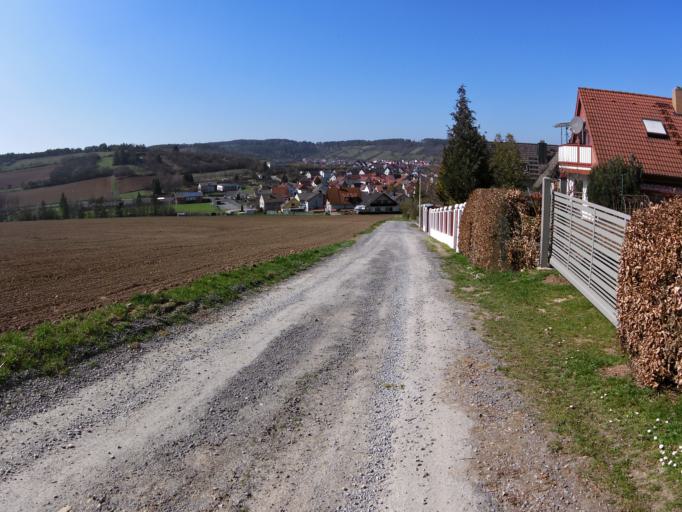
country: DE
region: Bavaria
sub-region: Regierungsbezirk Unterfranken
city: Erlabrunn
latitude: 49.8563
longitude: 9.8132
